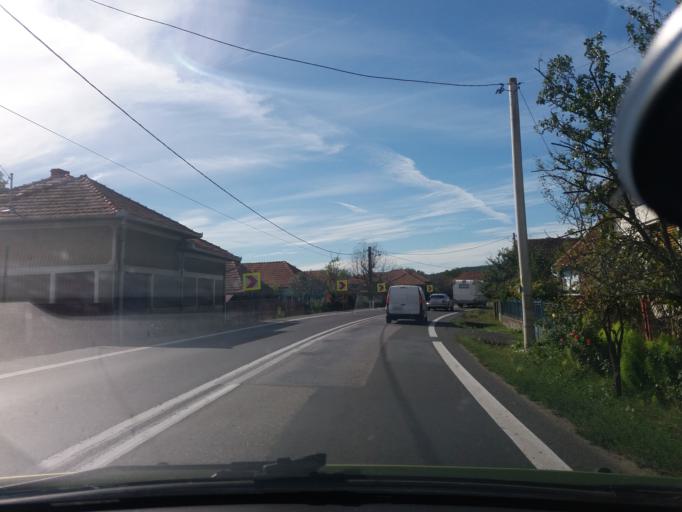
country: RO
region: Hunedoara
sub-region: Comuna Ilia
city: Ilia
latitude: 45.9441
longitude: 22.6095
